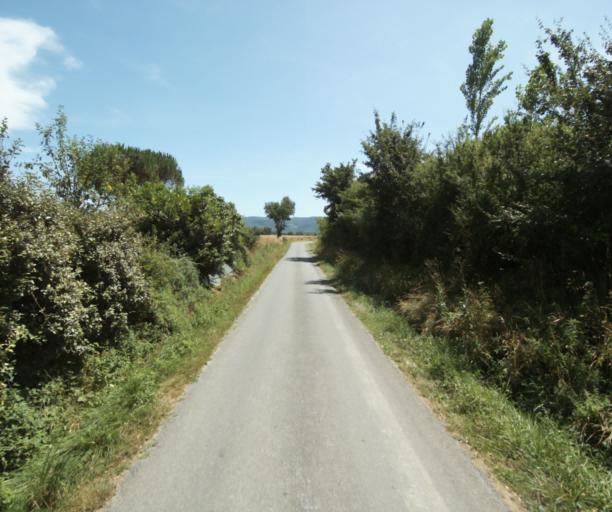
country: FR
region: Midi-Pyrenees
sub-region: Departement du Tarn
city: Soreze
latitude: 43.4884
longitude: 2.0558
